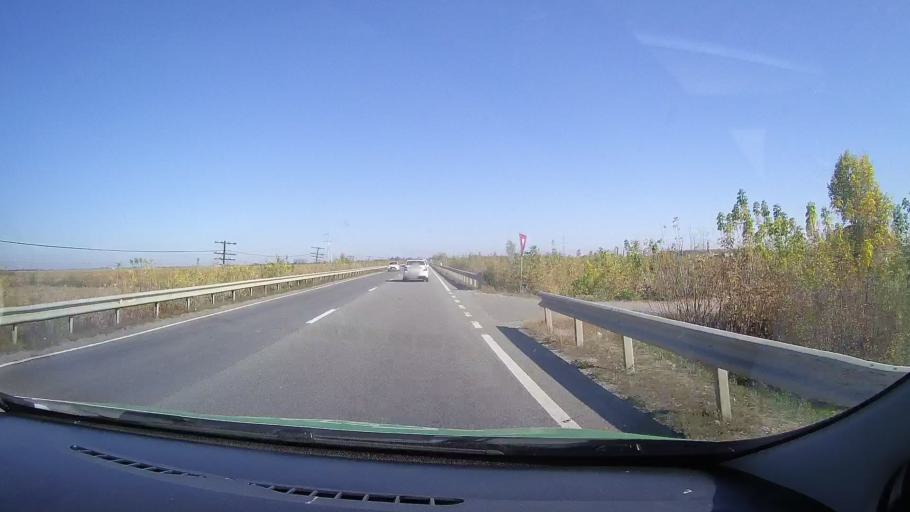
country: RO
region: Satu Mare
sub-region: Comuna Doba
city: Doba
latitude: 47.7334
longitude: 22.6922
